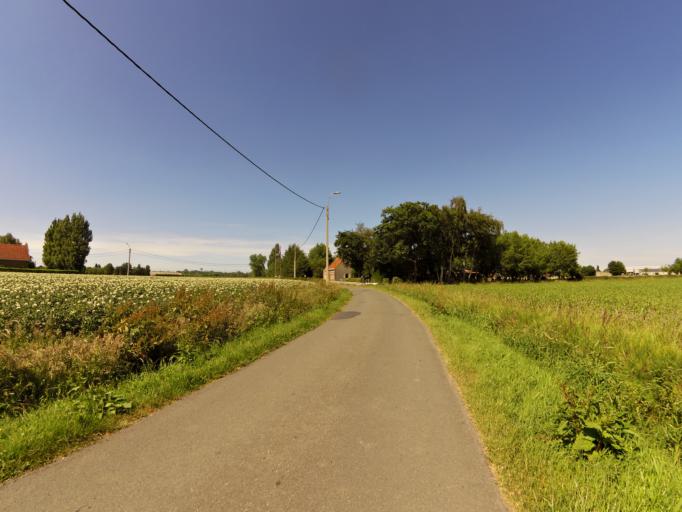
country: BE
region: Flanders
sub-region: Provincie West-Vlaanderen
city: Ichtegem
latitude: 51.1414
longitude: 3.0380
